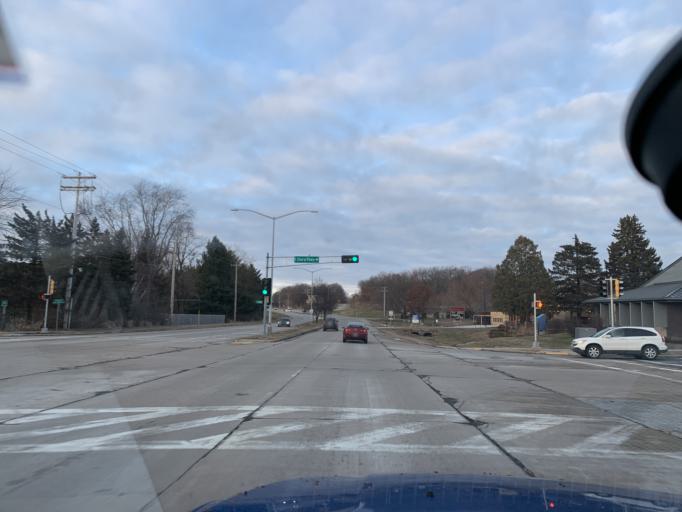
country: US
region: Wisconsin
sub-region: Dane County
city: Fitchburg
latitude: 43.0049
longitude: -89.4277
